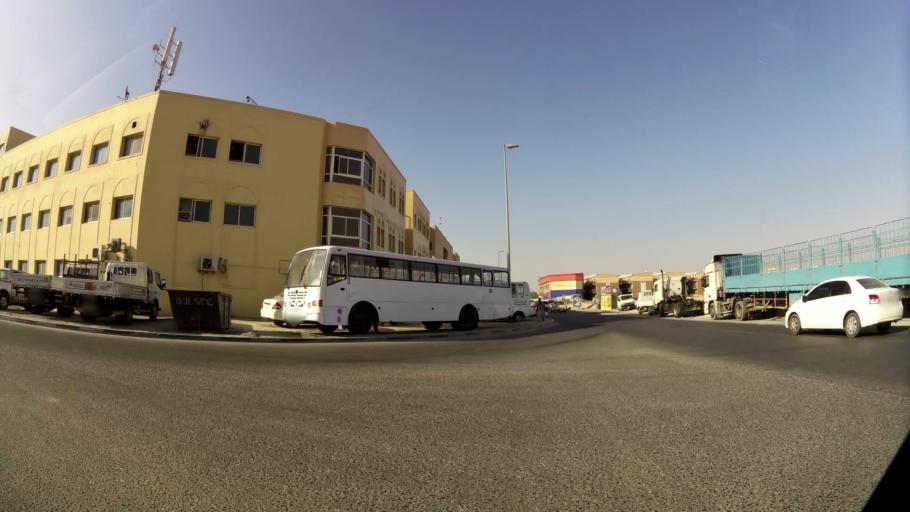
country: AE
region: Dubai
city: Dubai
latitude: 25.1256
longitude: 55.2347
